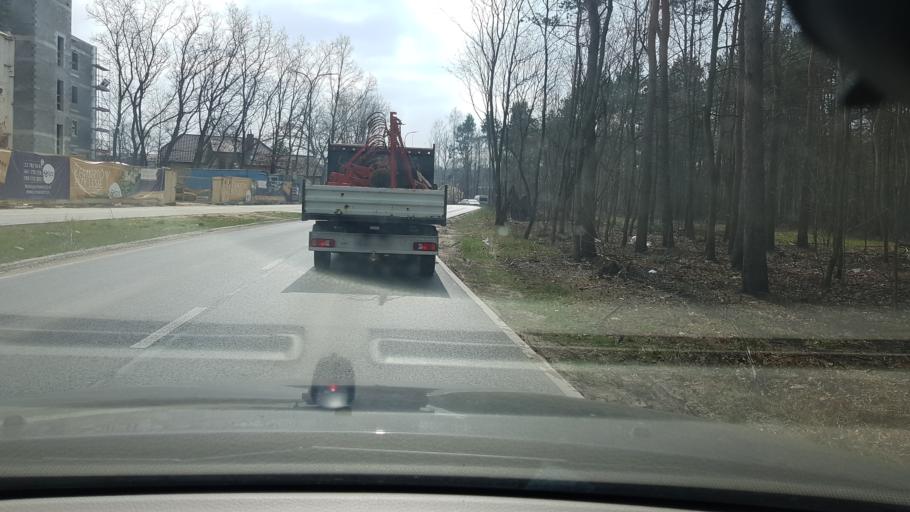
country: PL
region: Masovian Voivodeship
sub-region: Warszawa
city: Rembertow
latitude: 52.2603
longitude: 21.1514
